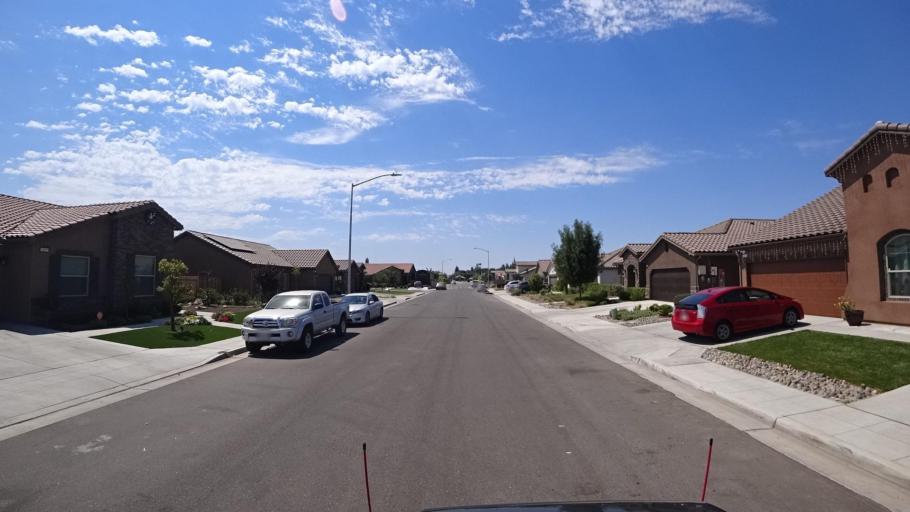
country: US
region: California
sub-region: Fresno County
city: Sunnyside
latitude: 36.7323
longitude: -119.7130
